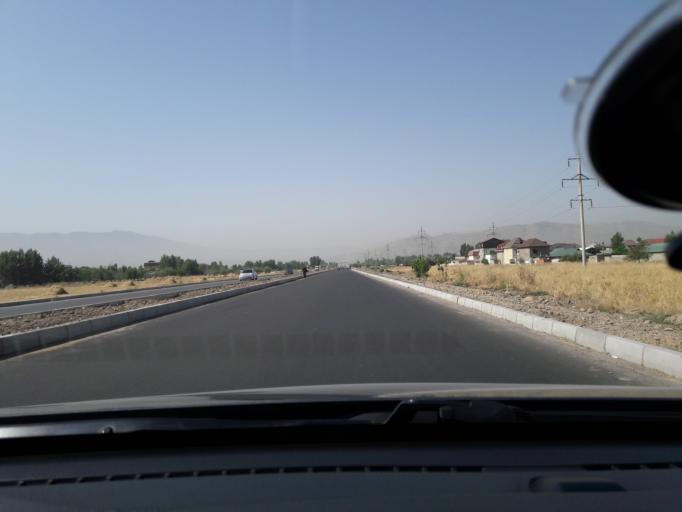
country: TJ
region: Dushanbe
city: Dushanbe
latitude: 38.4944
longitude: 68.7533
